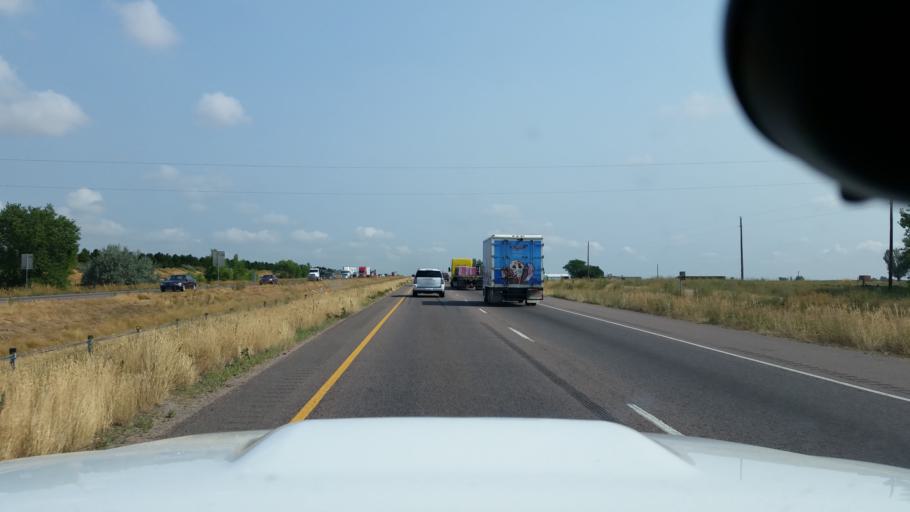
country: US
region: Colorado
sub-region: Weld County
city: Mead
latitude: 40.2474
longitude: -104.9801
